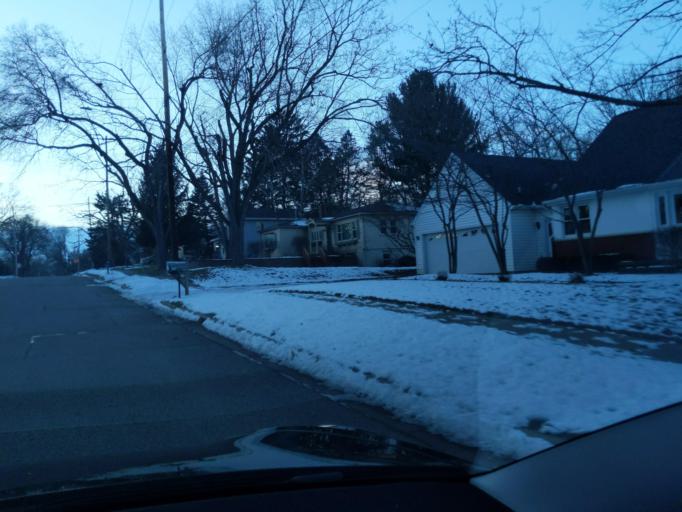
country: US
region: Michigan
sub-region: Ingham County
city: Mason
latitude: 42.5750
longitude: -84.4464
